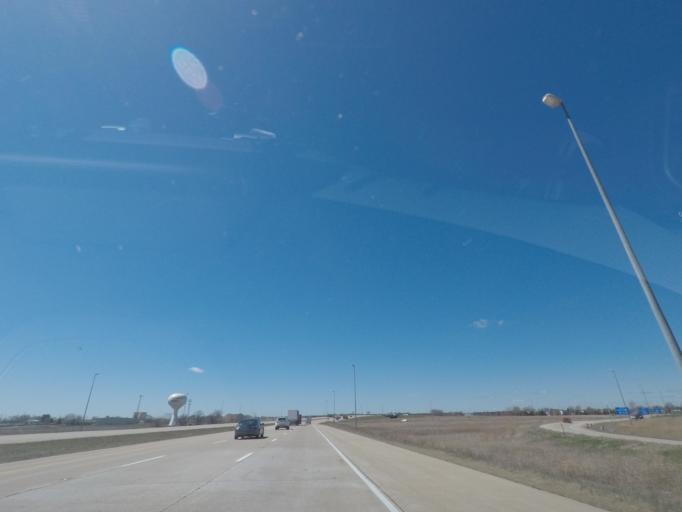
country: US
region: Illinois
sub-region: McLean County
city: Normal
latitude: 40.5392
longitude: -88.9406
